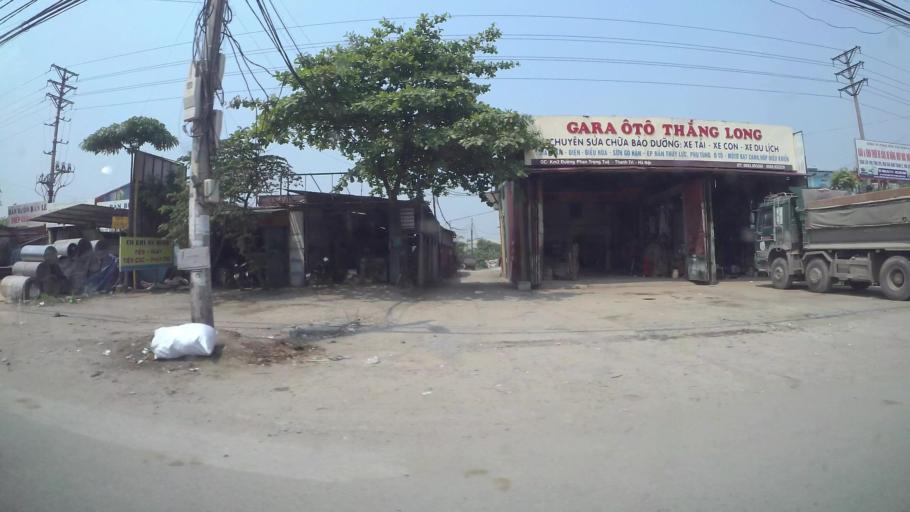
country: VN
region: Ha Noi
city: Van Dien
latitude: 20.9471
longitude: 105.8271
